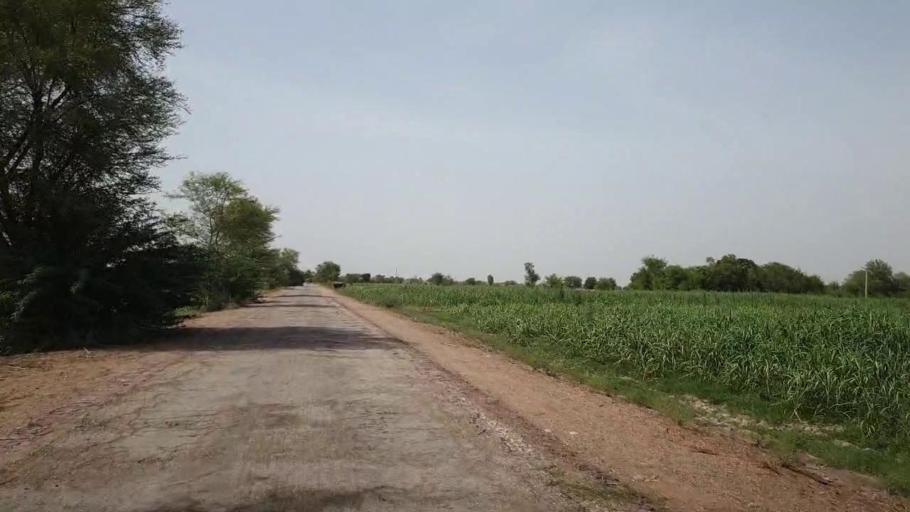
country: PK
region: Sindh
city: Daur
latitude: 26.5344
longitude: 68.4076
